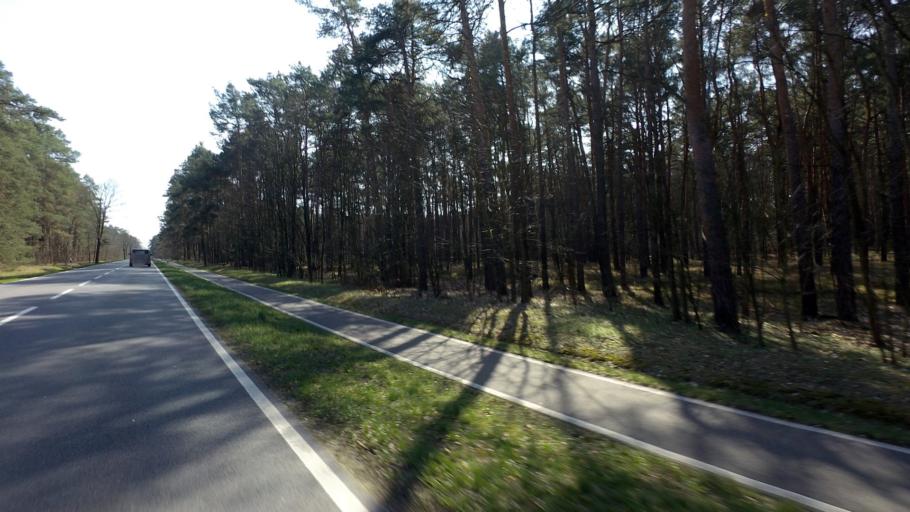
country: DE
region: Brandenburg
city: Baruth
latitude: 52.0371
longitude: 13.5195
